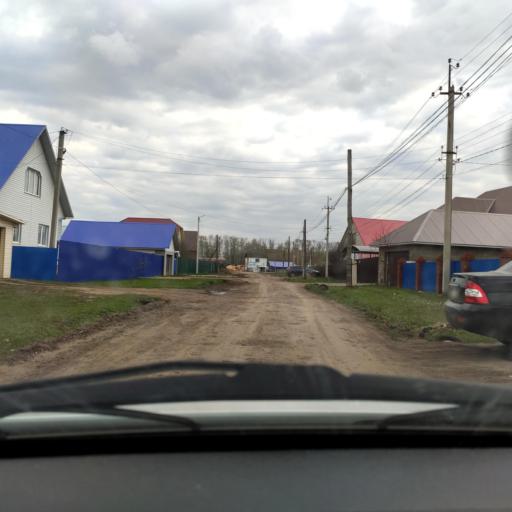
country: RU
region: Bashkortostan
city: Iglino
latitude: 54.8220
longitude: 56.3804
